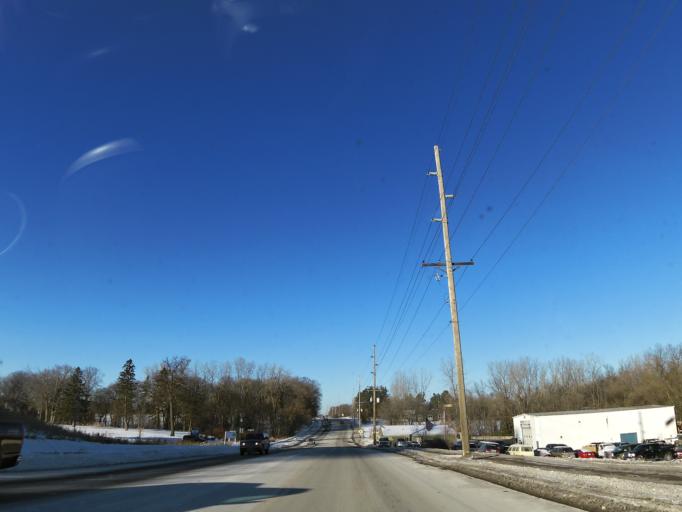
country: US
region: Minnesota
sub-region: Hennepin County
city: Mound
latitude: 44.9486
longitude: -93.6656
